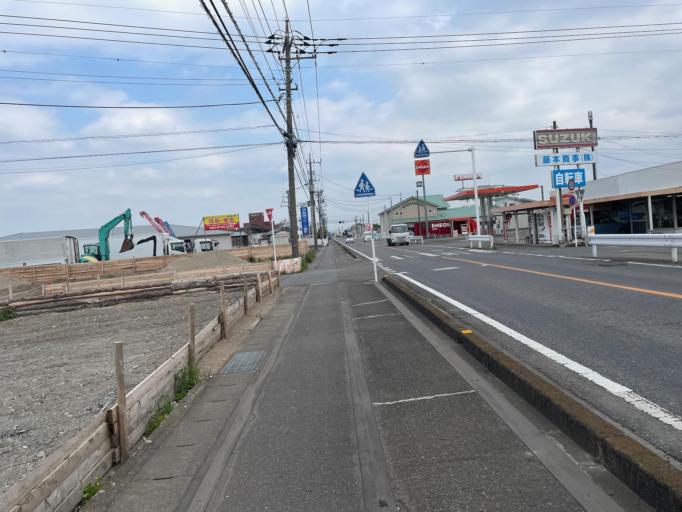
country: JP
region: Gunma
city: Isesaki
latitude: 36.2871
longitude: 139.1881
